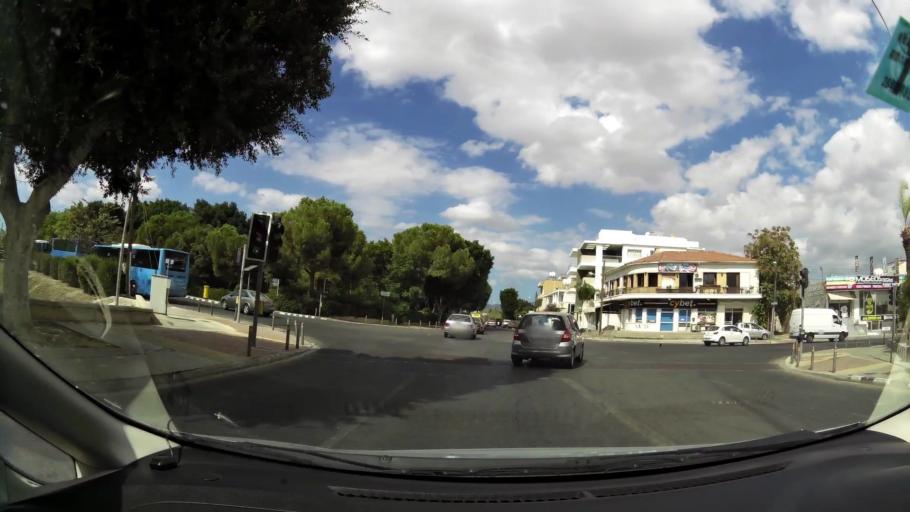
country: CY
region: Lefkosia
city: Nicosia
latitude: 35.1756
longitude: 33.3729
